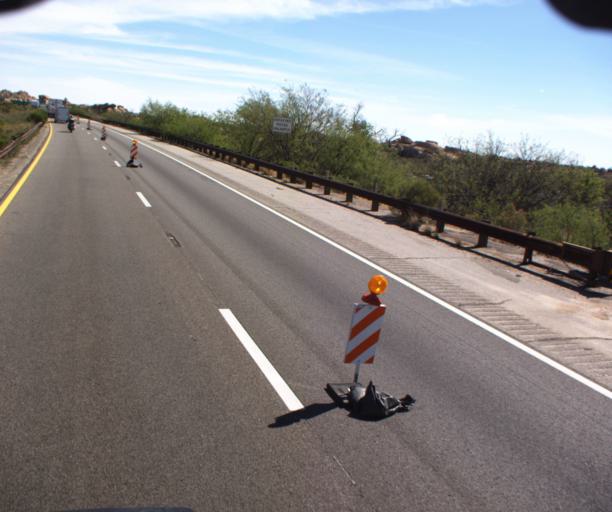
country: US
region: Arizona
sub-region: Cochise County
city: Saint David
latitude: 32.0421
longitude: -110.0936
